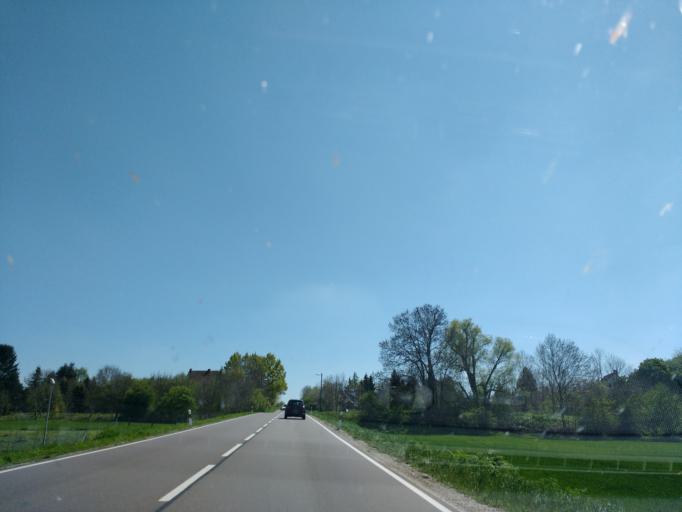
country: DE
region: Saxony-Anhalt
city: Deuben
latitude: 51.1290
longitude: 12.0590
